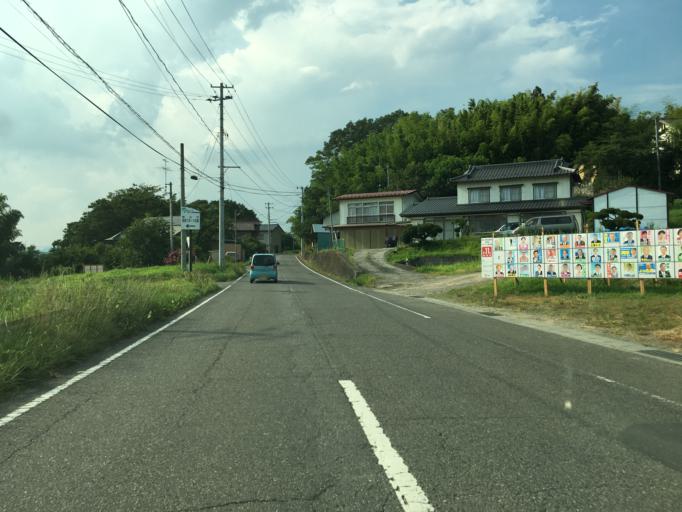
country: JP
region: Fukushima
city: Motomiya
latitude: 37.4585
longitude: 140.4246
